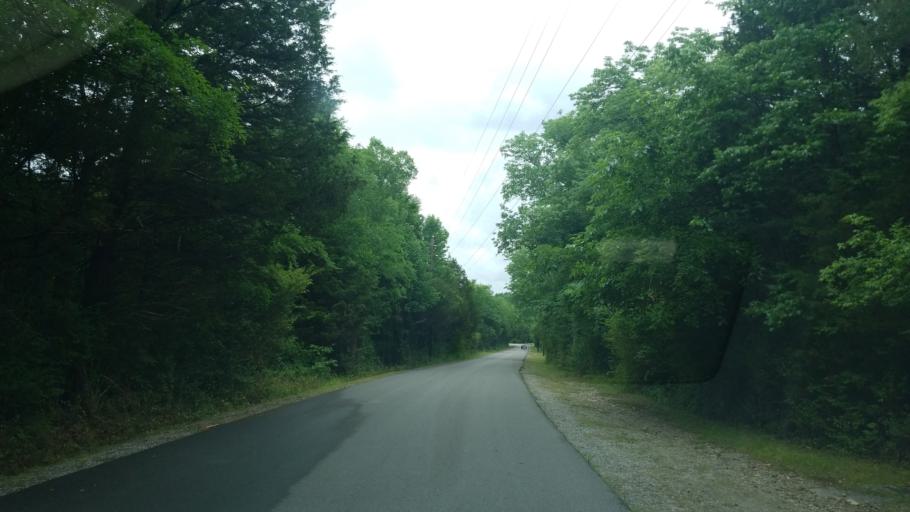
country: US
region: Tennessee
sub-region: Rutherford County
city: La Vergne
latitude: 36.1077
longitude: -86.6273
